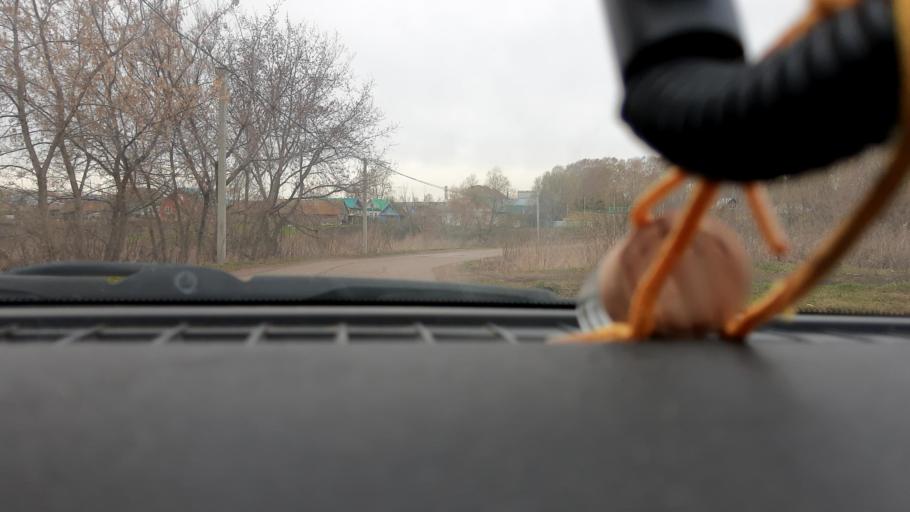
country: RU
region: Bashkortostan
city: Asanovo
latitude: 54.8139
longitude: 55.5654
